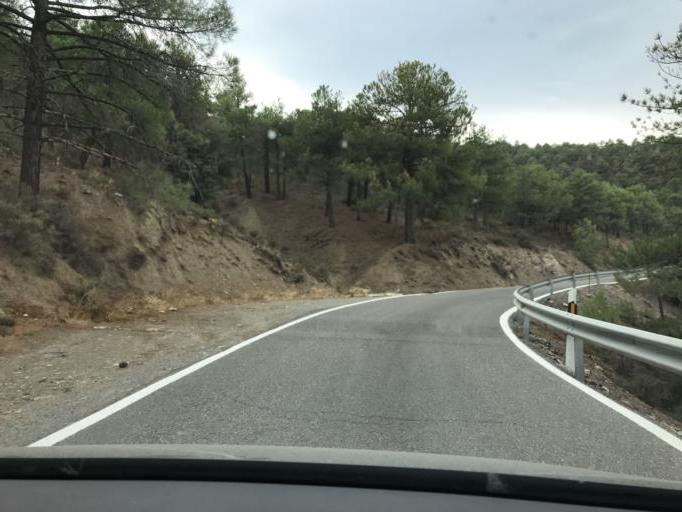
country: ES
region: Andalusia
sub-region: Provincia de Granada
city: Ferreira
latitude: 37.1624
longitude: -3.0518
